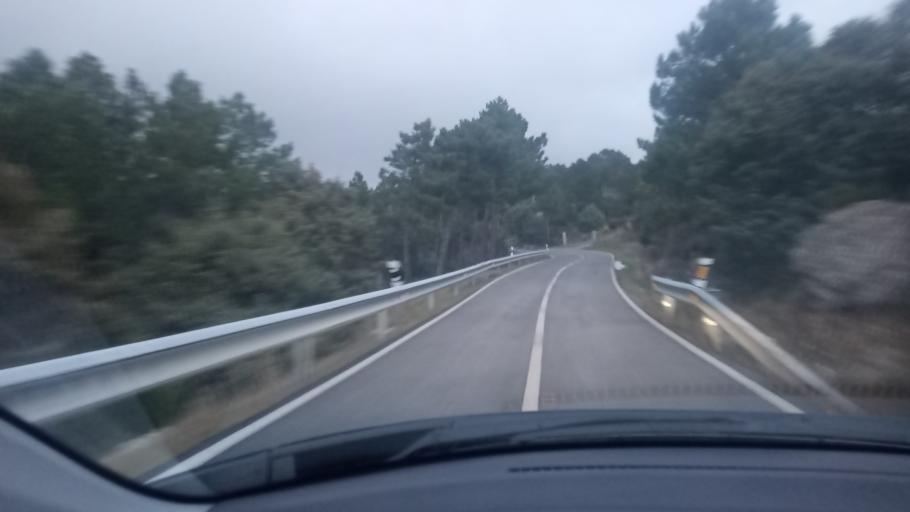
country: ES
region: Madrid
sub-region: Provincia de Madrid
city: Zarzalejo
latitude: 40.5522
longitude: -4.1952
